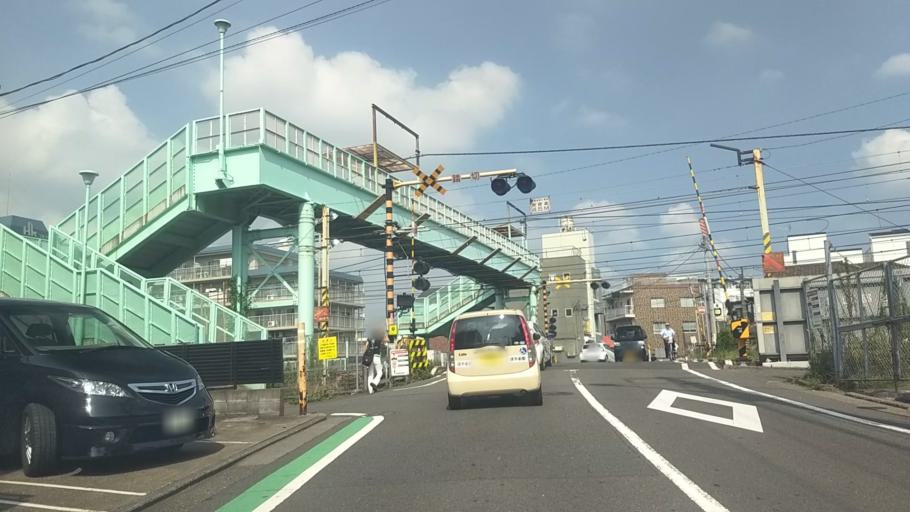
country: JP
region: Kanagawa
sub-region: Kawasaki-shi
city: Kawasaki
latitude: 35.5205
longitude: 139.6848
